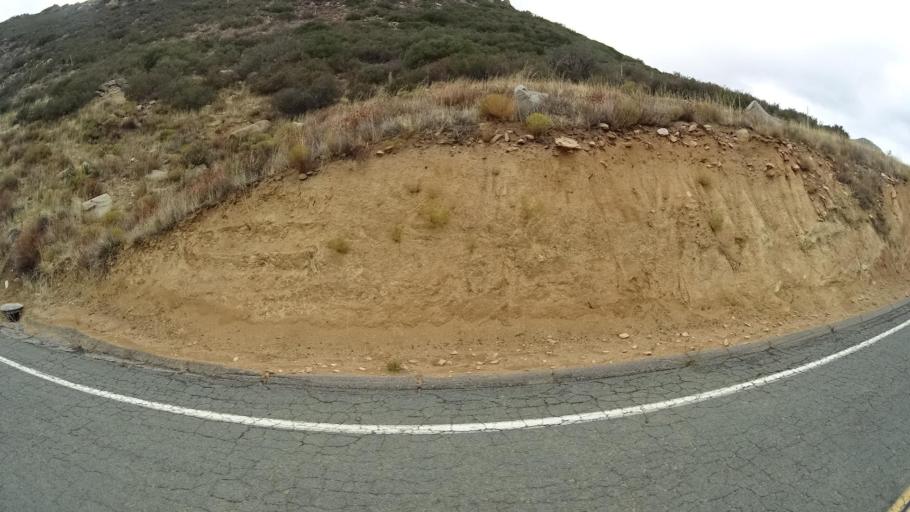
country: US
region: California
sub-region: San Diego County
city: Pine Valley
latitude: 32.7592
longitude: -116.4516
